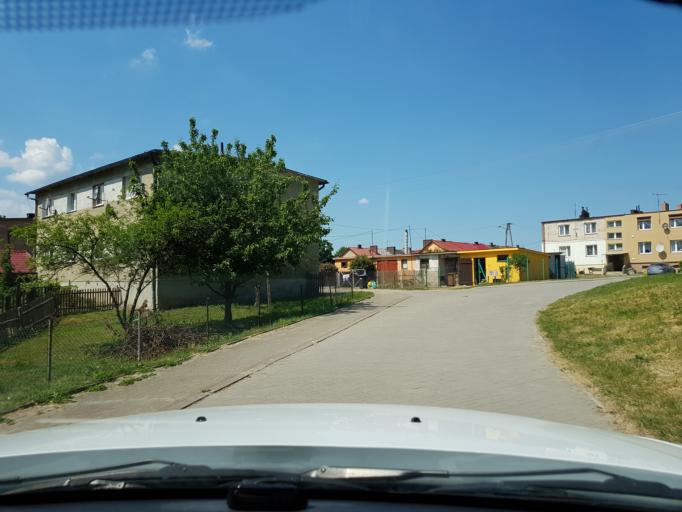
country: PL
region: West Pomeranian Voivodeship
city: Trzcinsko Zdroj
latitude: 52.9123
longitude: 14.5941
